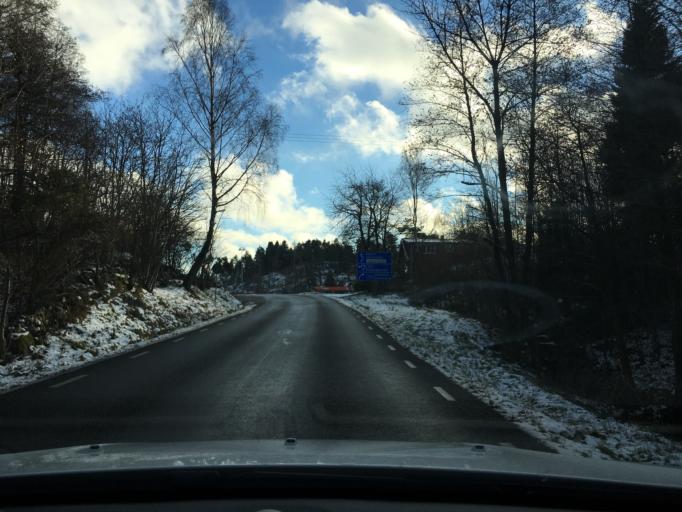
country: SE
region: Vaestra Goetaland
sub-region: Tjorns Kommun
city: Myggenas
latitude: 58.0398
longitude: 11.7336
